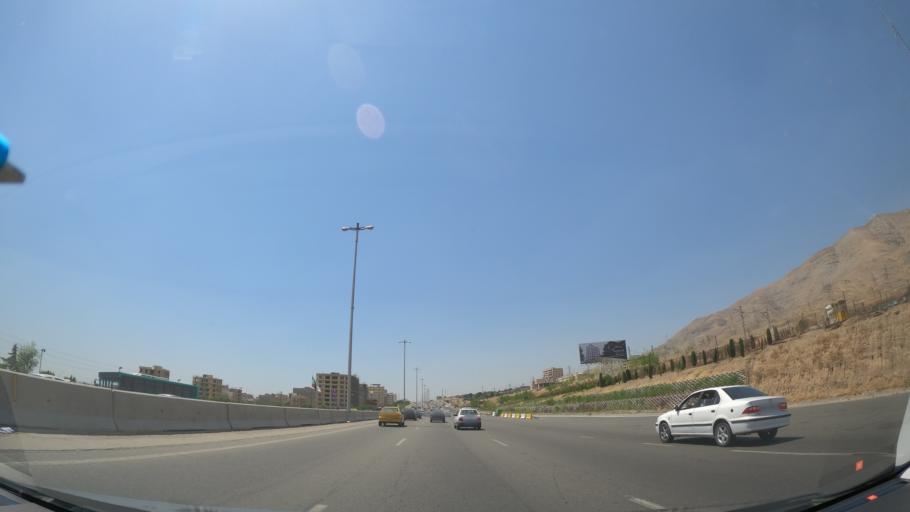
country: IR
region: Tehran
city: Shahr-e Qods
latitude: 35.7540
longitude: 51.0753
